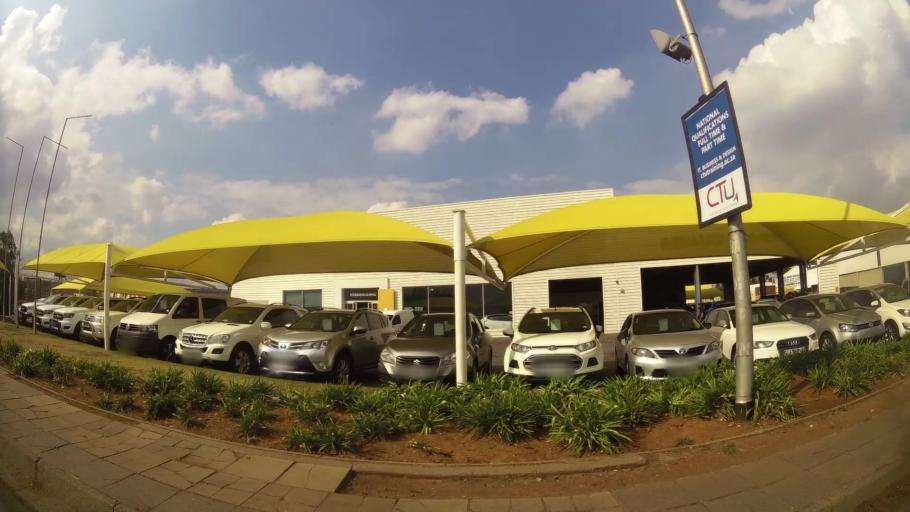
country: ZA
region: Gauteng
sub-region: Sedibeng District Municipality
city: Vereeniging
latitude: -26.6648
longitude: 27.9341
